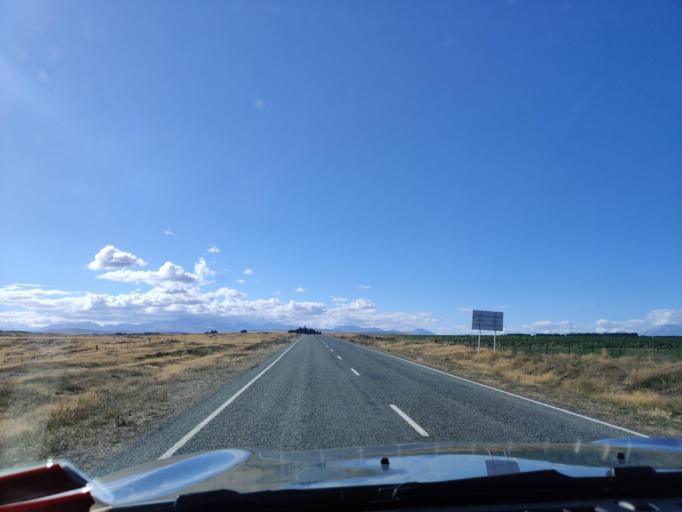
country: NZ
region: Canterbury
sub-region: Timaru District
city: Pleasant Point
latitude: -44.1104
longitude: 170.3529
